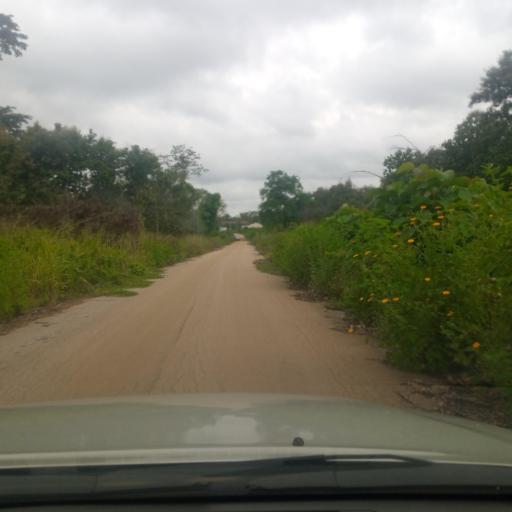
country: NG
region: Ebonyi
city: Effium
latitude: 6.6271
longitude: 8.0509
